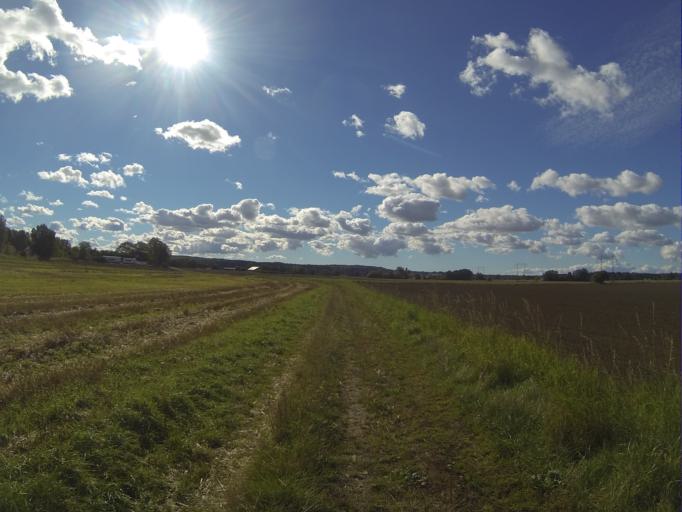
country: SE
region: Skane
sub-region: Lunds Kommun
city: Genarp
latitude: 55.7244
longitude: 13.3881
